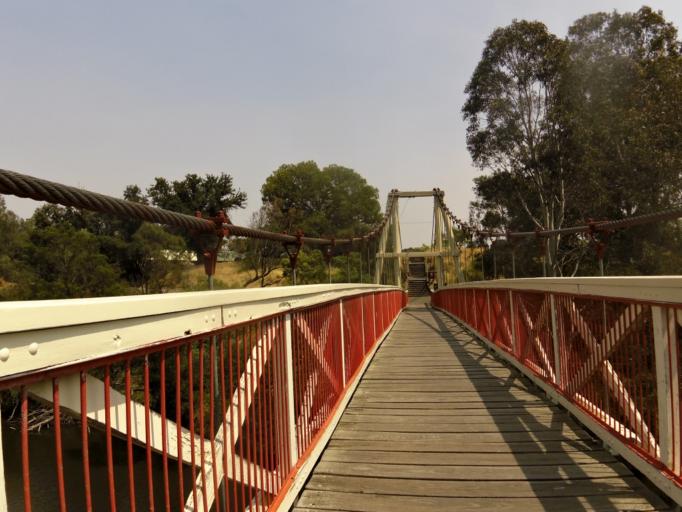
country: AU
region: Victoria
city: Abbotsford
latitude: -37.8000
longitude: 145.0097
